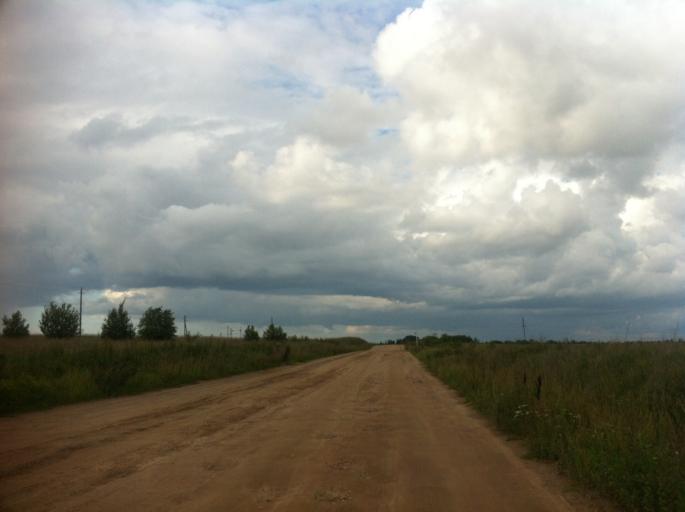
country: RU
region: Pskov
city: Izborsk
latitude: 57.8250
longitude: 27.9802
